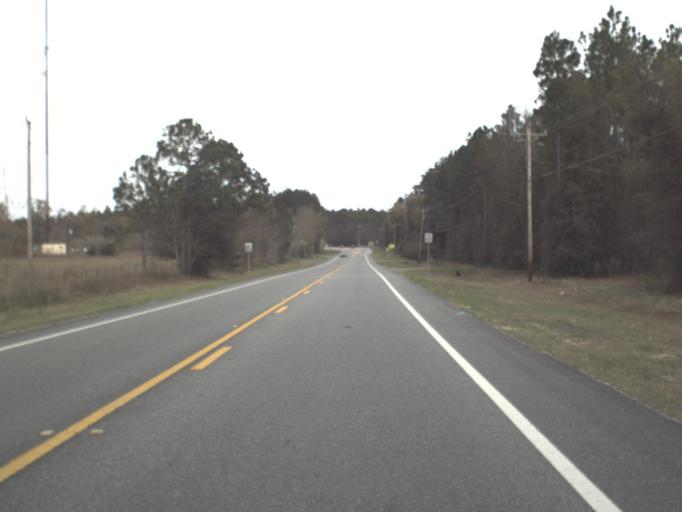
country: US
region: Florida
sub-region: Wakulla County
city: Crawfordville
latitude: 30.2610
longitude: -84.3584
